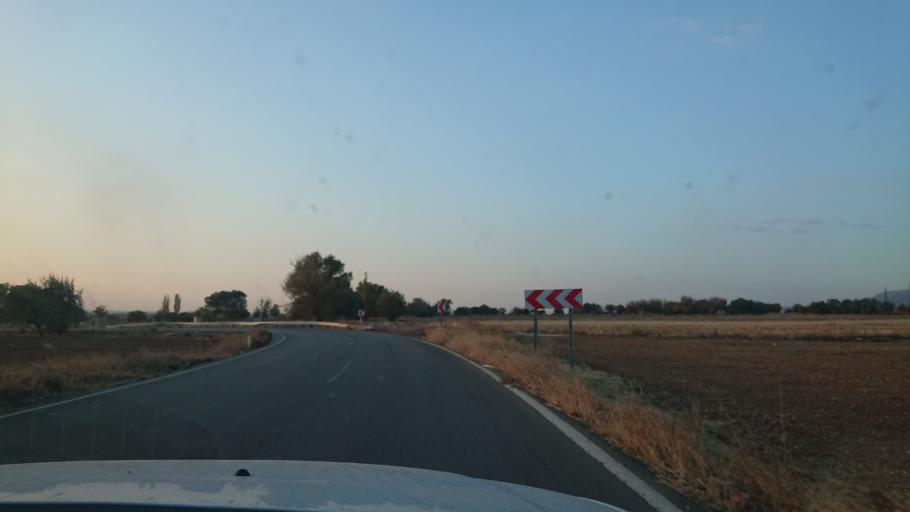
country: TR
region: Aksaray
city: Aksaray
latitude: 38.3006
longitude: 34.0824
